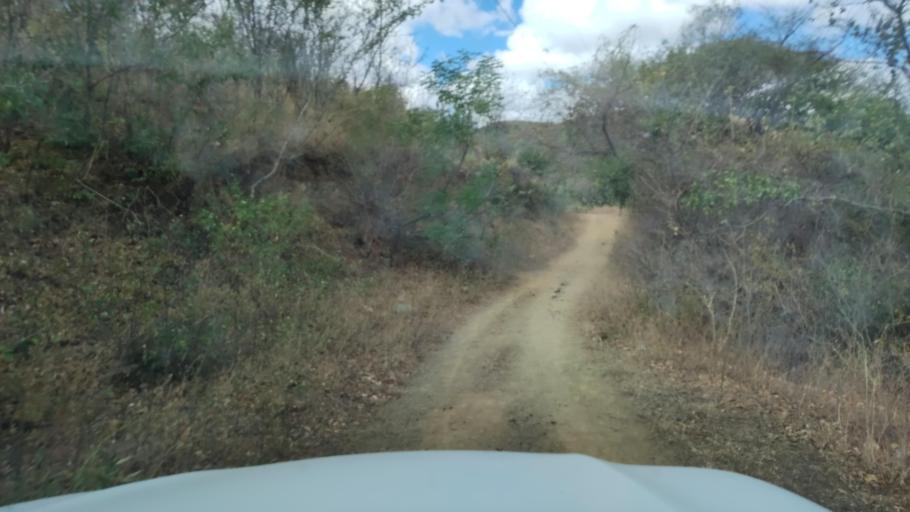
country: NI
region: Carazo
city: Santa Teresa
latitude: 11.6432
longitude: -86.2182
